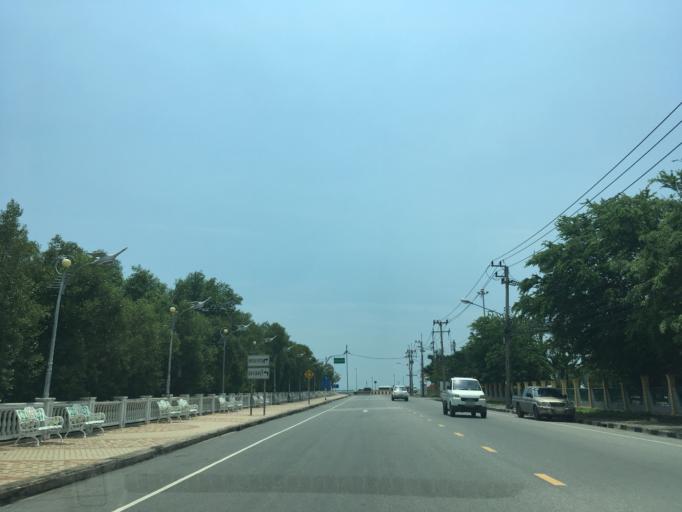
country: TH
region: Chon Buri
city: Chon Buri
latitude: 13.3617
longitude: 100.9761
